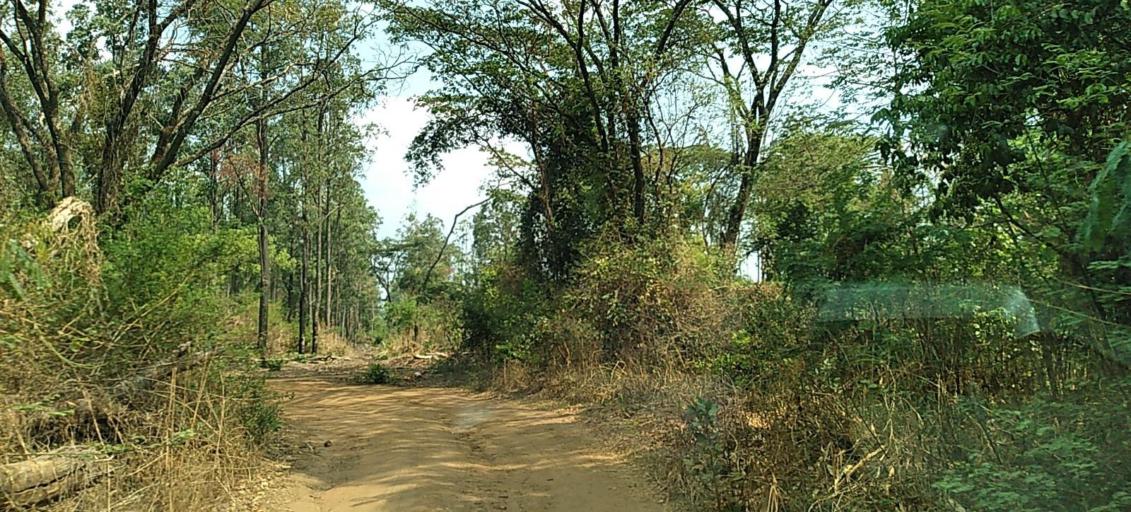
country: ZM
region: Copperbelt
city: Chingola
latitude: -12.7408
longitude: 27.7605
